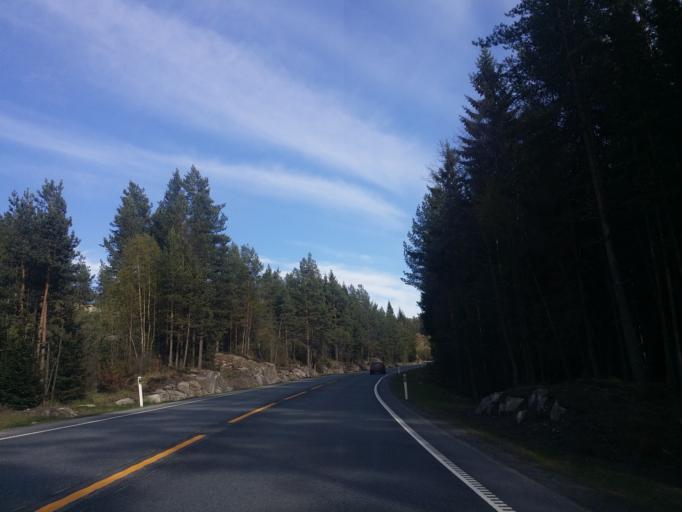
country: NO
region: Telemark
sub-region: Notodden
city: Notodden
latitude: 59.5842
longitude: 9.3098
